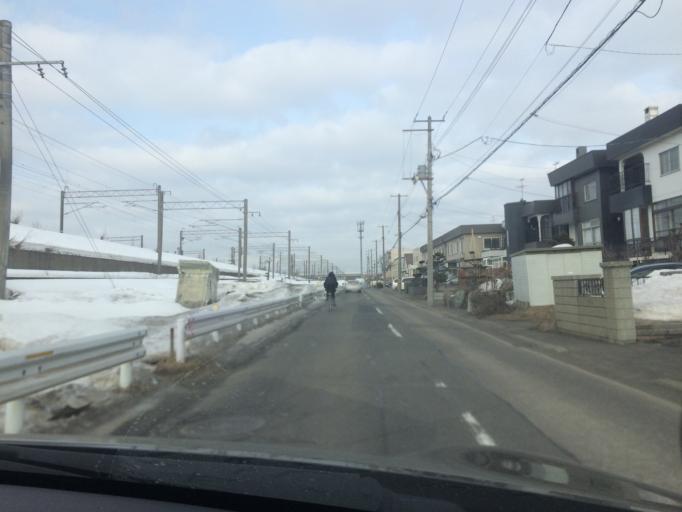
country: JP
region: Hokkaido
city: Sapporo
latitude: 43.0451
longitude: 141.4483
